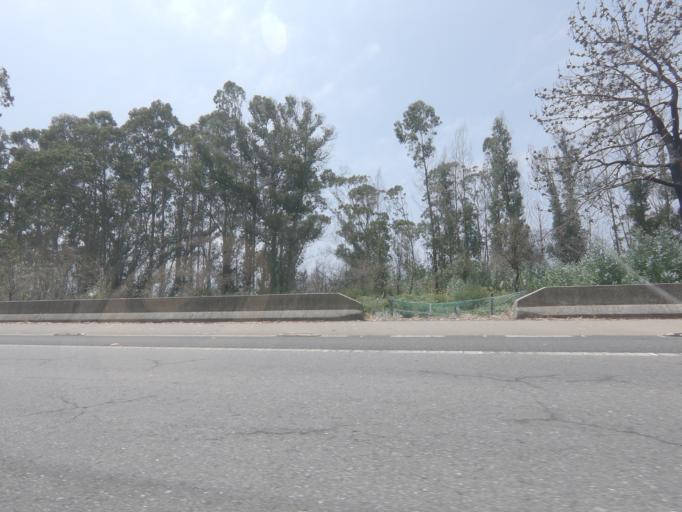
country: ES
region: Galicia
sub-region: Provincia de Pontevedra
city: A Guarda
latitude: 41.9265
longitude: -8.8812
